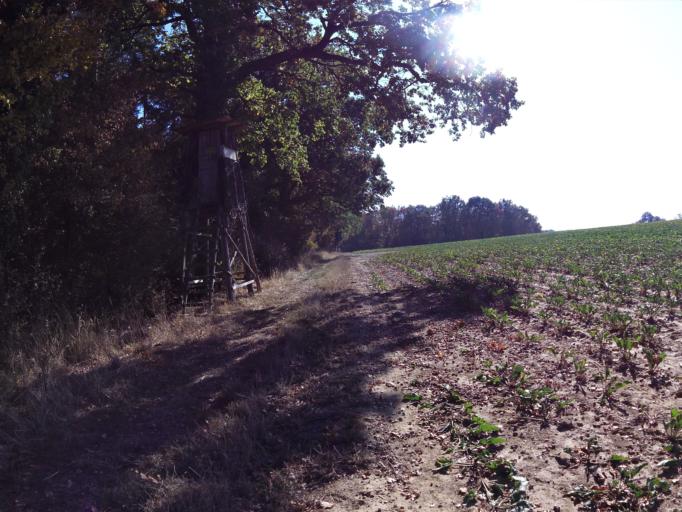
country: DE
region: Bavaria
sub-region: Regierungsbezirk Unterfranken
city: Eibelstadt
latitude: 49.7254
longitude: 9.9803
